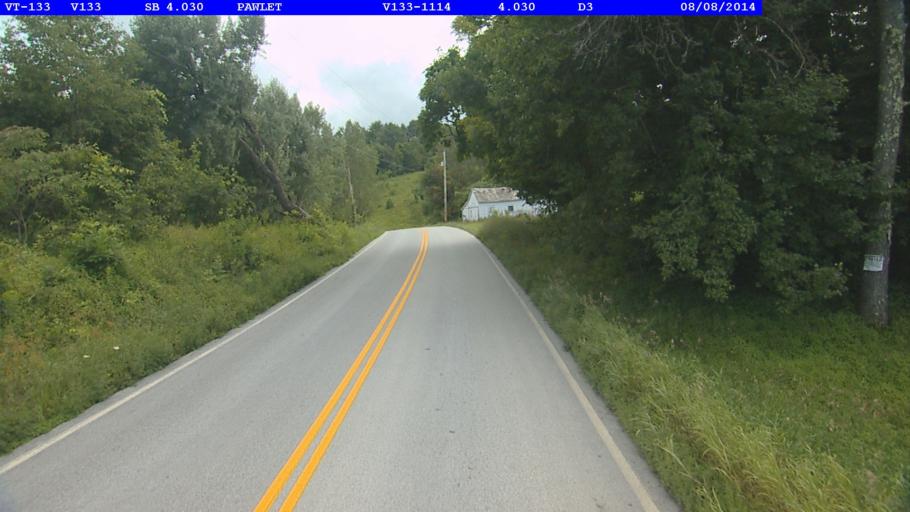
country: US
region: New York
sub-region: Washington County
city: Granville
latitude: 43.3876
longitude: -73.1361
